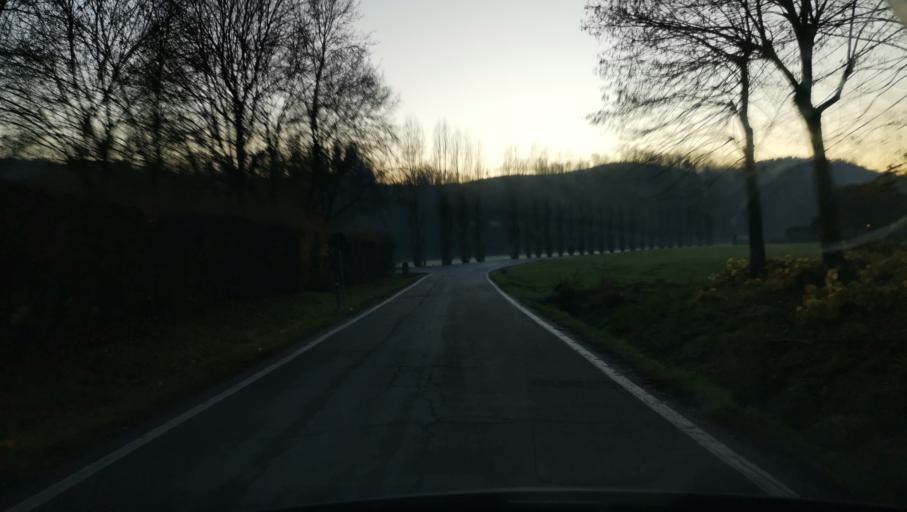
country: IT
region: Piedmont
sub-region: Provincia di Torino
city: Rivalba
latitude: 45.1094
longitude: 7.8956
